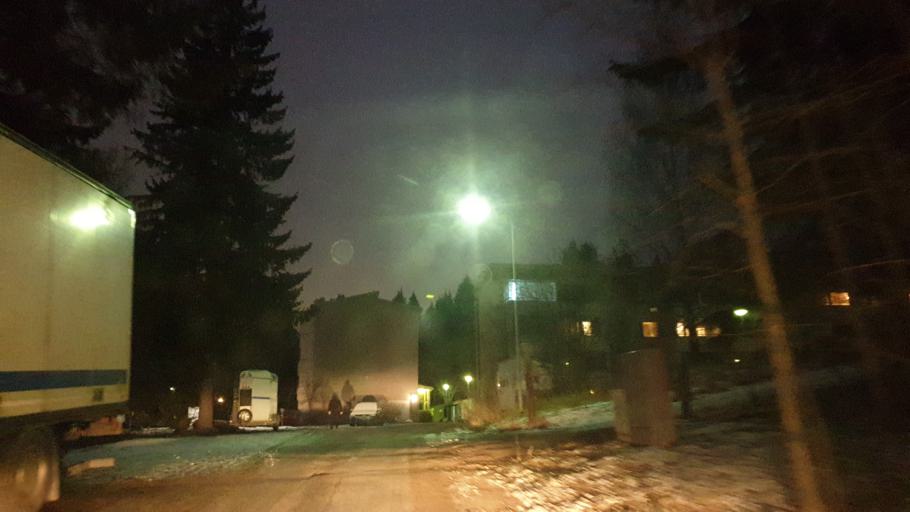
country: FI
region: Southern Savonia
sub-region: Savonlinna
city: Savonlinna
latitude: 61.8604
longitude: 28.9528
